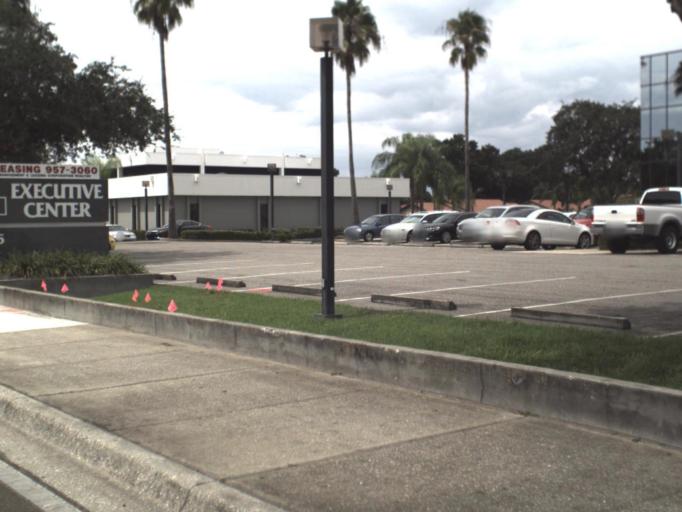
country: US
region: Florida
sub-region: Sarasota County
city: South Gate Ridge
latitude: 27.2989
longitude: -82.4947
